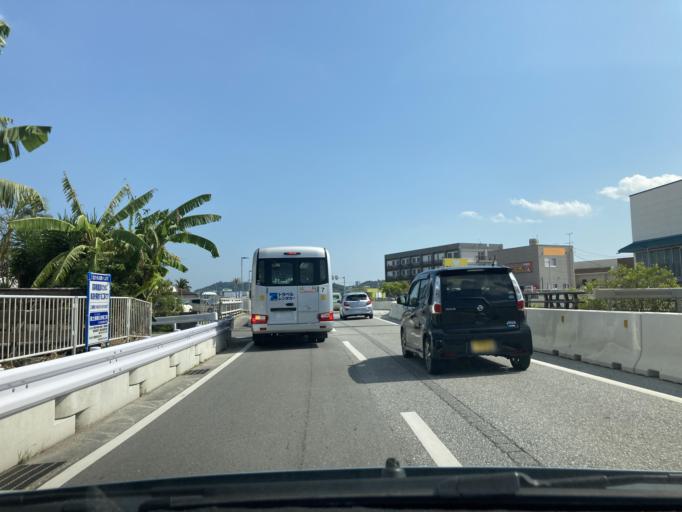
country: JP
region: Okinawa
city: Tomigusuku
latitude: 26.1736
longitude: 127.6567
